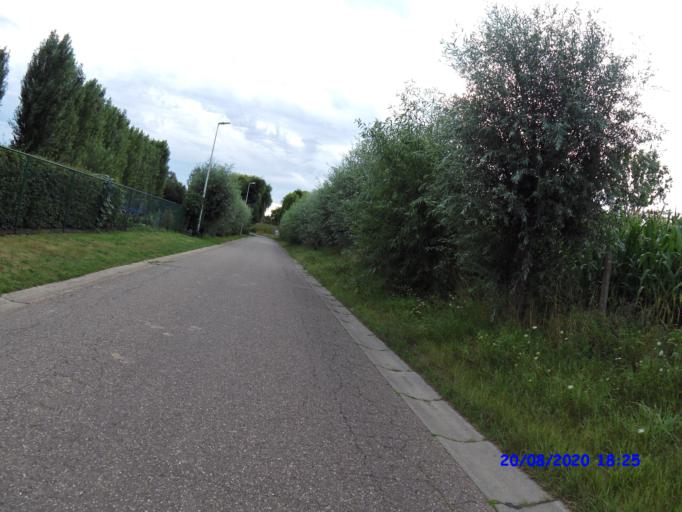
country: BE
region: Flanders
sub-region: Provincie Limburg
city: Nieuwerkerken
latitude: 50.8456
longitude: 5.1985
